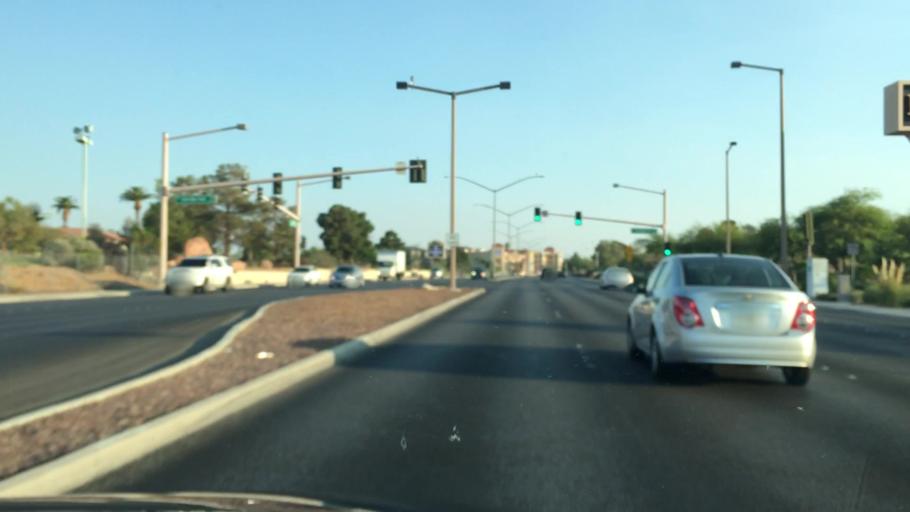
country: US
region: Nevada
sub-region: Clark County
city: Summerlin South
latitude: 36.1746
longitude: -115.2872
